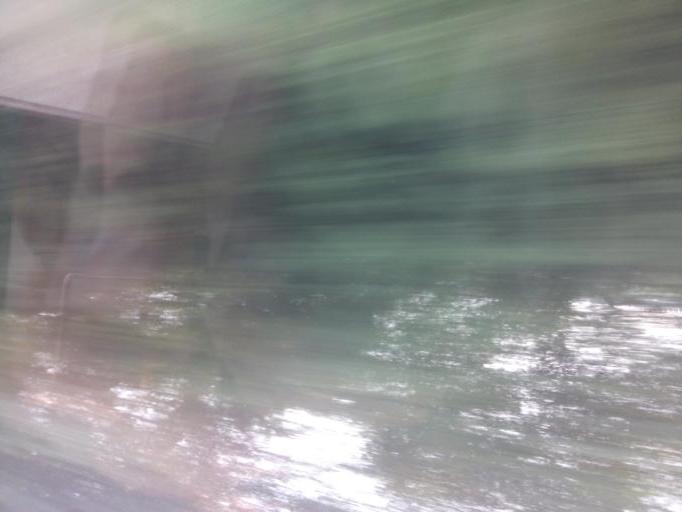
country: GB
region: England
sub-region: Kirklees
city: Marsden
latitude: 53.6175
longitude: -1.8991
